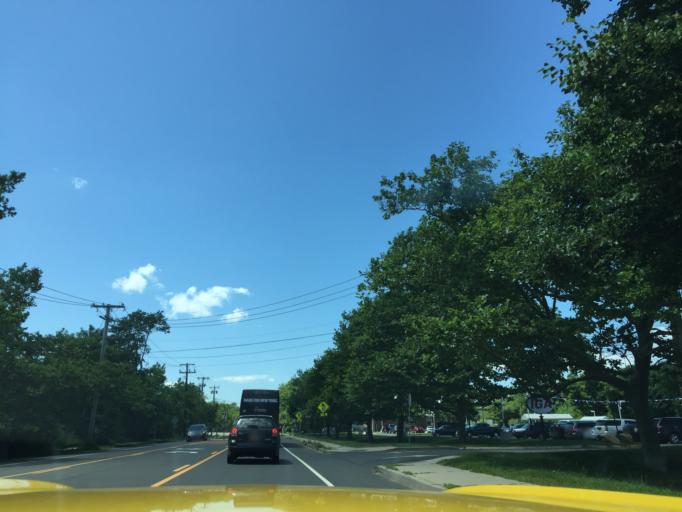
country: US
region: New York
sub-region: Suffolk County
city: Amagansett
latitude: 40.9787
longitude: -72.1271
